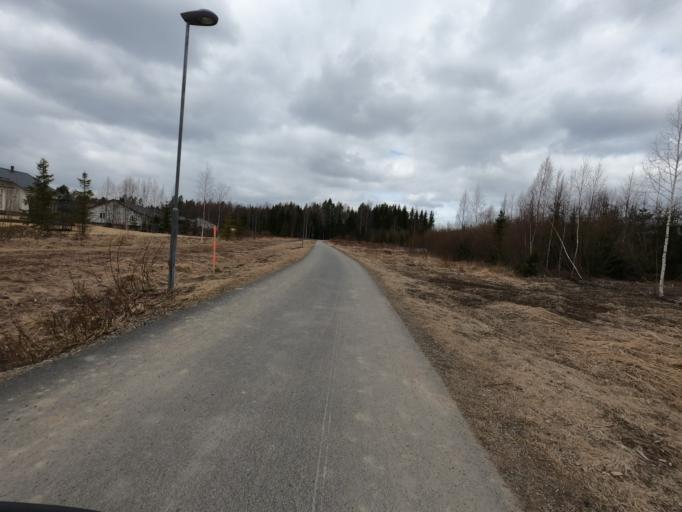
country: FI
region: North Karelia
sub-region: Joensuu
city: Joensuu
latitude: 62.5682
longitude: 29.8161
